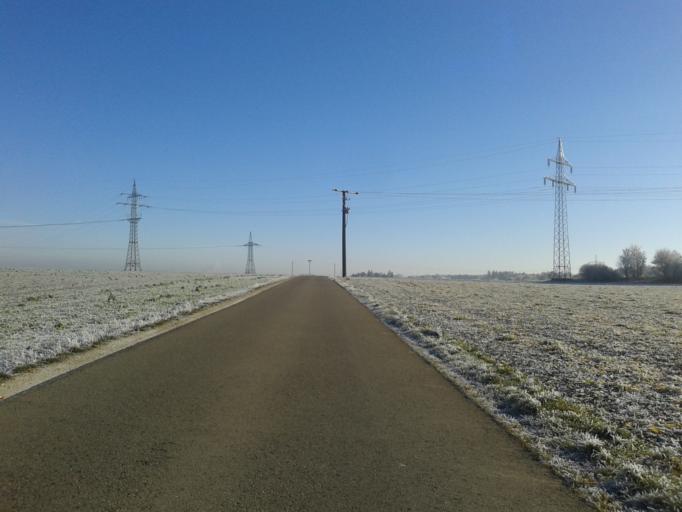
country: DE
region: Baden-Wuerttemberg
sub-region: Tuebingen Region
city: Beimerstetten
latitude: 48.4589
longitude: 9.9896
